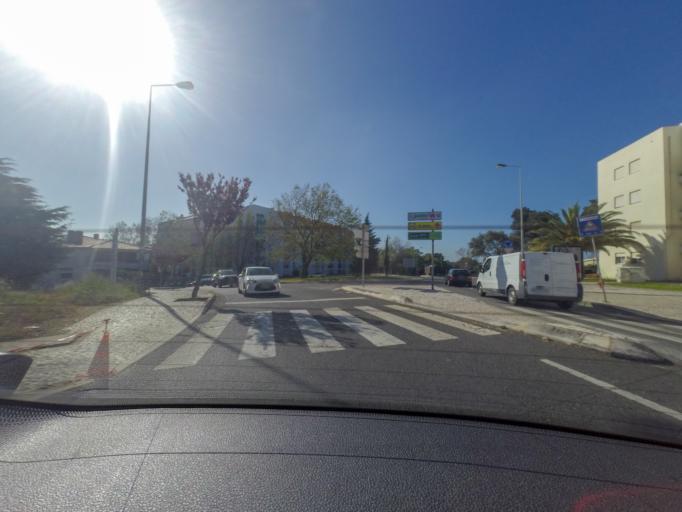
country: PT
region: Lisbon
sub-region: Cascais
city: Monte Estoril
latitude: 38.7153
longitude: -9.4178
